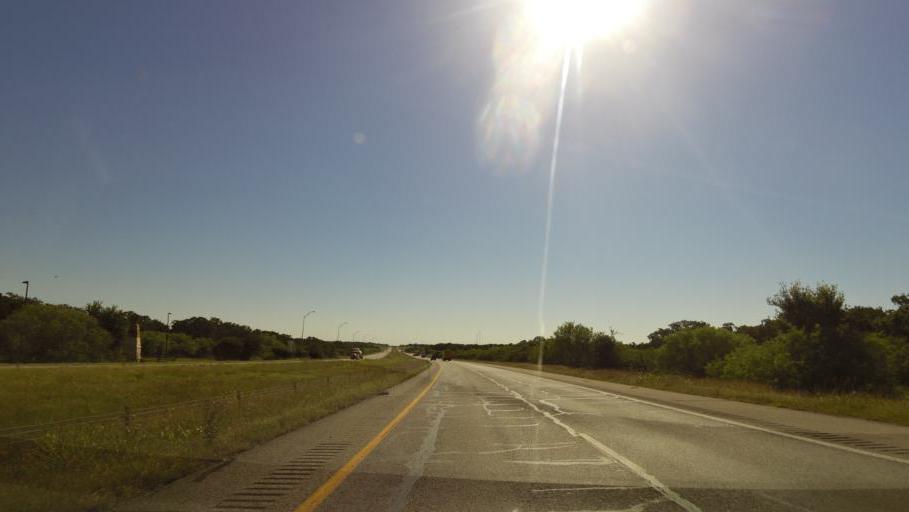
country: US
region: Texas
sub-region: Guadalupe County
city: Seguin
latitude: 29.6152
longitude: -97.8048
